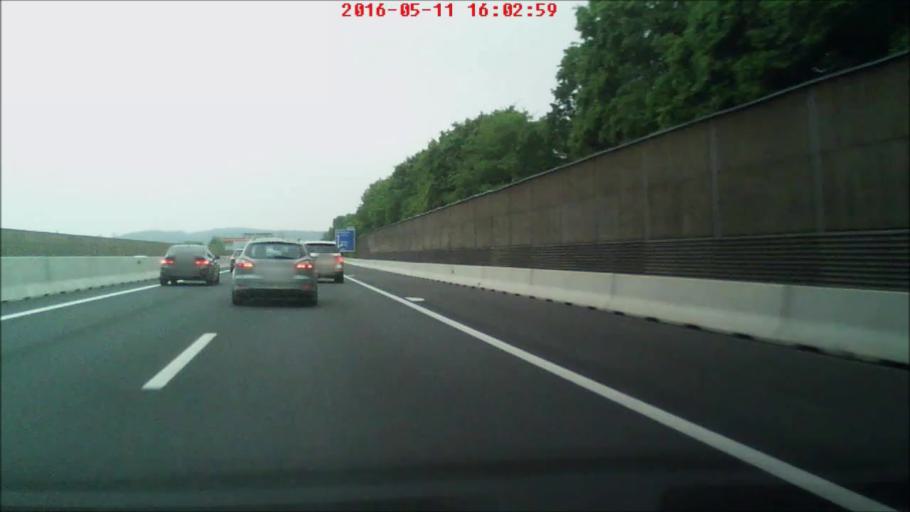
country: AT
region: Styria
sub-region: Politischer Bezirk Leibnitz
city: Weitendorf
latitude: 46.9060
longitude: 15.4722
